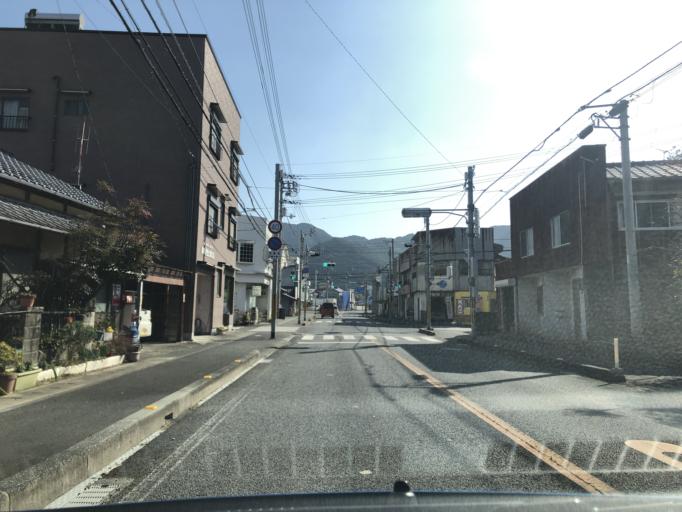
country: JP
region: Kochi
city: Sukumo
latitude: 32.9379
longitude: 132.7225
